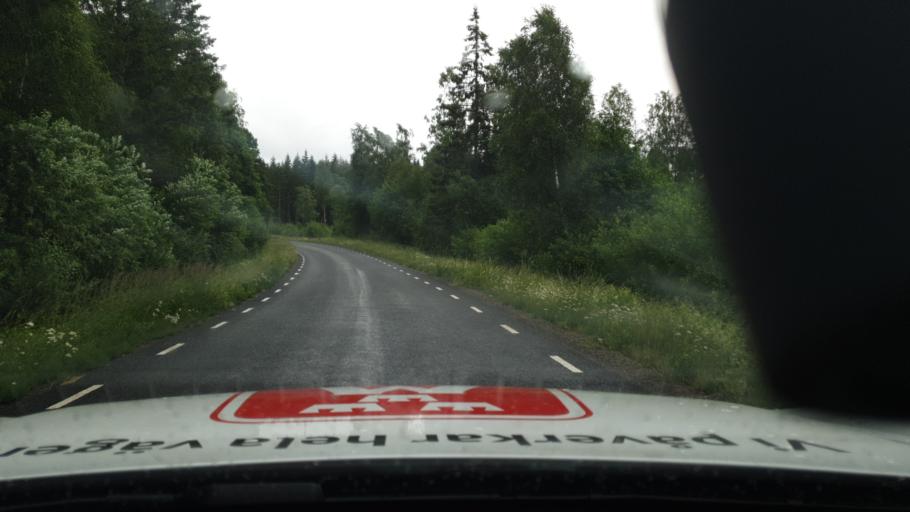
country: SE
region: Joenkoeping
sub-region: Mullsjo Kommun
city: Mullsjoe
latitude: 58.0099
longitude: 13.7033
